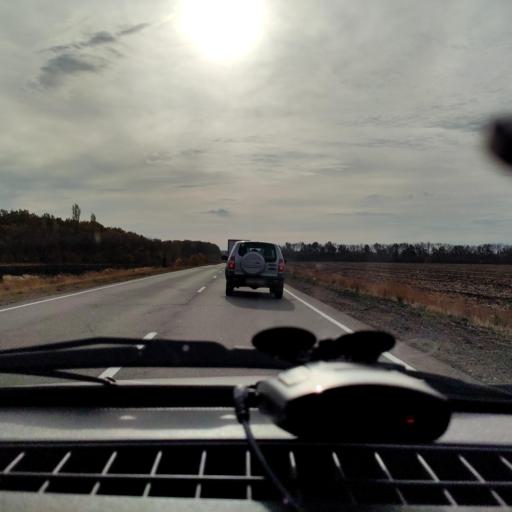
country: RU
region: Voronezj
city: Shilovo
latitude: 51.4366
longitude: 39.0005
